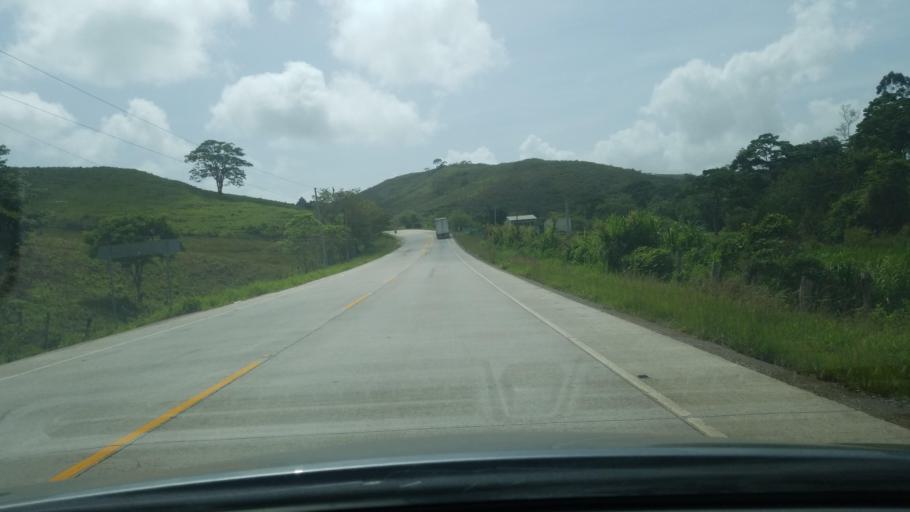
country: HN
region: Copan
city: San Jeronimo
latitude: 14.9347
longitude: -88.9247
